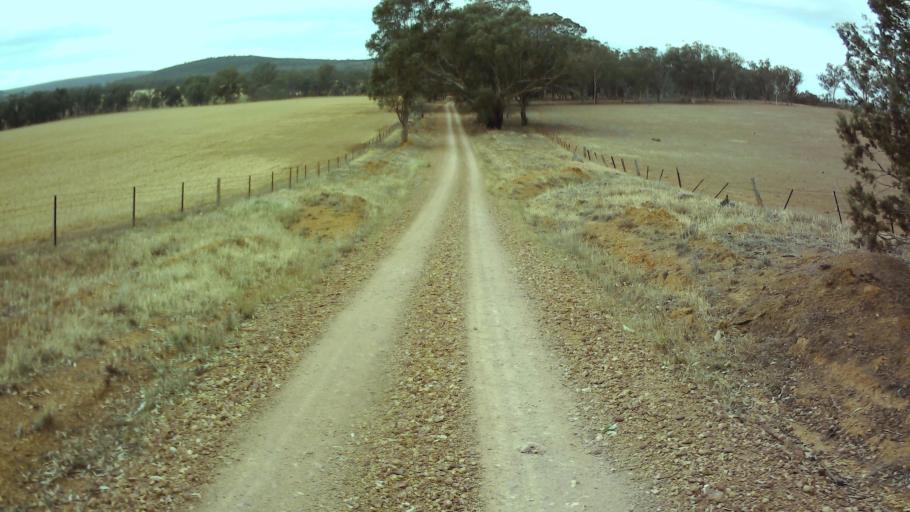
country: AU
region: New South Wales
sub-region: Weddin
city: Grenfell
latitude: -33.9278
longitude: 148.2557
